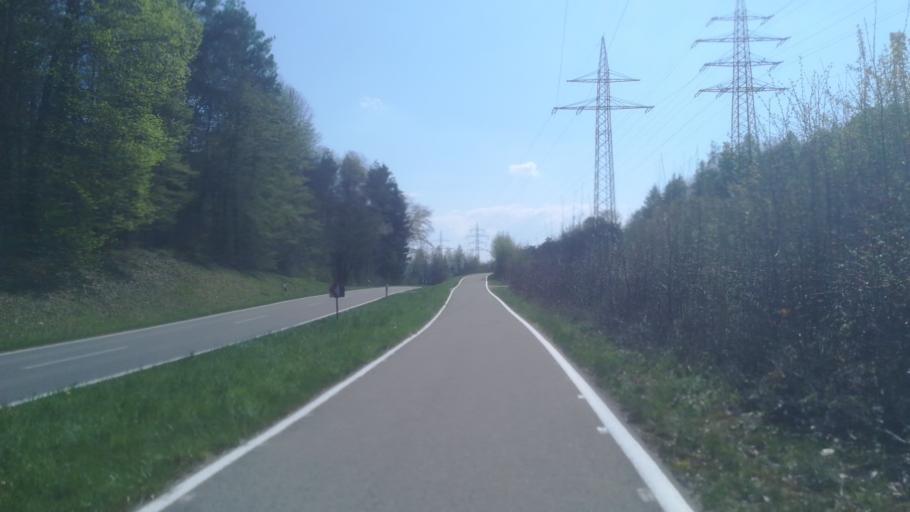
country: DE
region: Baden-Wuerttemberg
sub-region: Freiburg Region
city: Singen
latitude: 47.7761
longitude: 8.8634
